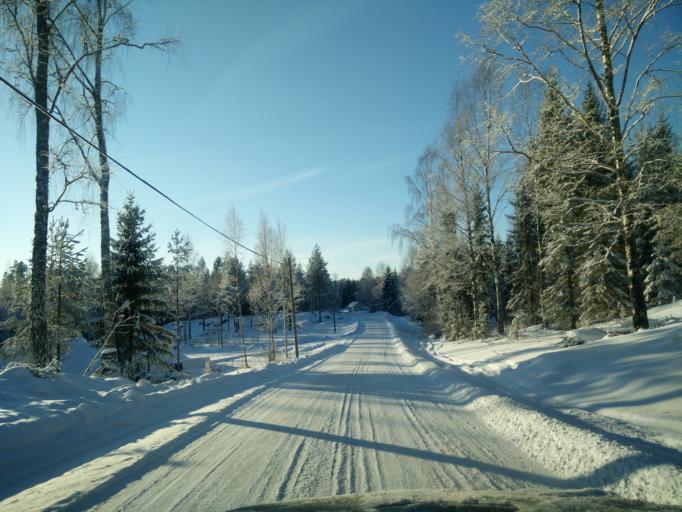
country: SE
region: Vaesternorrland
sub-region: Sundsvalls Kommun
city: Njurundabommen
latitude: 62.2332
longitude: 17.5104
